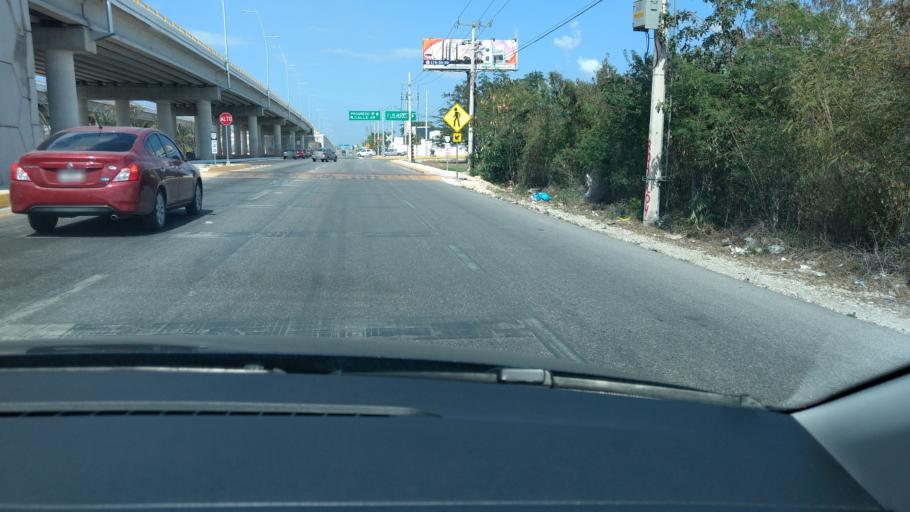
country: MX
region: Yucatan
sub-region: Kanasin
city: Kanasin
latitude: 20.9808
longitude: -89.5636
